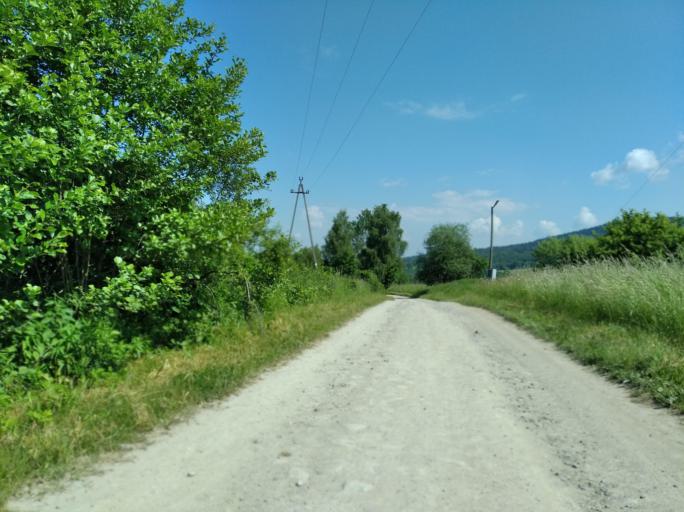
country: PL
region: Subcarpathian Voivodeship
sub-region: Powiat krosnienski
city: Odrzykon
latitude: 49.7735
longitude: 21.7614
